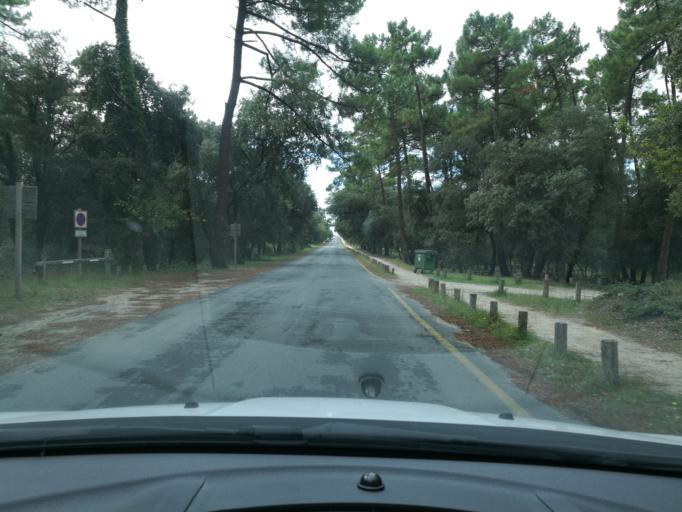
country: FR
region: Poitou-Charentes
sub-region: Departement de la Charente-Maritime
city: Saint-Trojan-les-Bains
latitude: 45.8582
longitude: -1.2425
